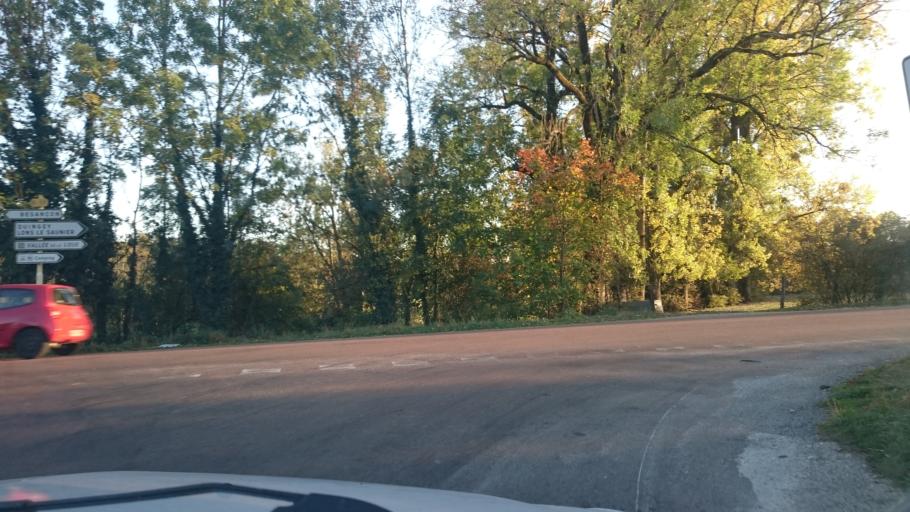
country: FR
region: Franche-Comte
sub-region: Departement du Doubs
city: Quingey
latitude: 47.1060
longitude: 5.8897
